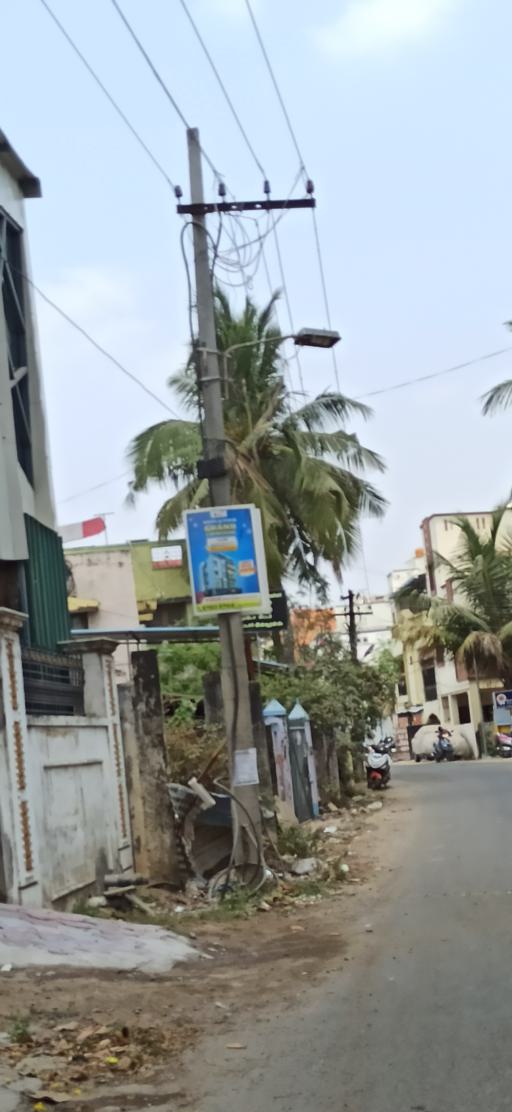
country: IN
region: Tamil Nadu
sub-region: Thiruvallur
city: Porur
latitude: 13.0183
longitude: 80.1437
